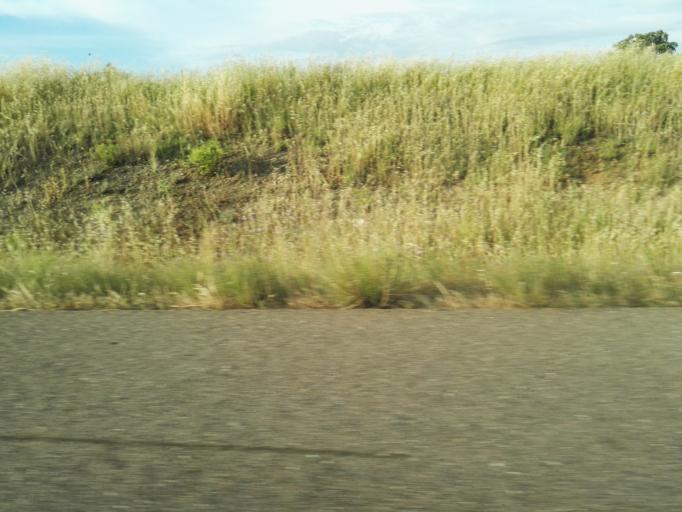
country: PT
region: Portalegre
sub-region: Elvas
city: Elvas
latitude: 38.8943
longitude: -7.1201
